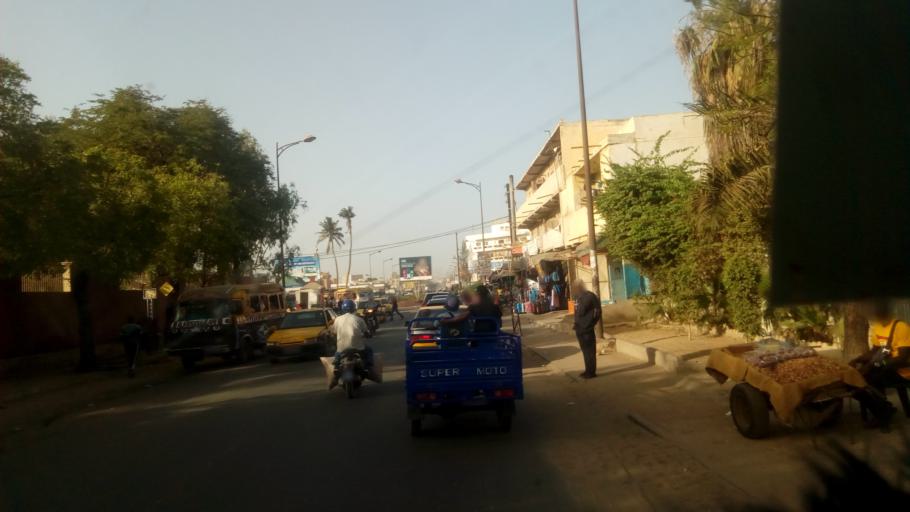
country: SN
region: Dakar
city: Dakar
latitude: 14.6977
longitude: -17.4474
